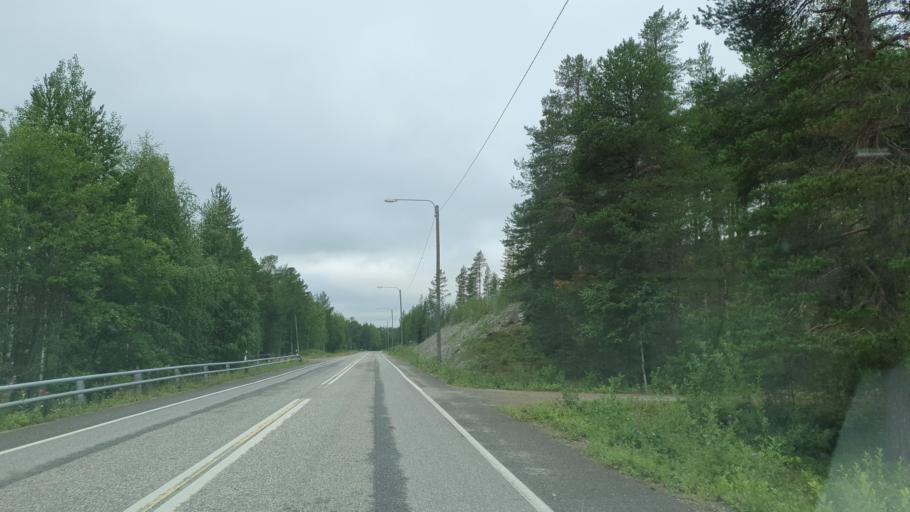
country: FI
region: Lapland
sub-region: Pohjois-Lappi
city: Sodankylae
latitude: 67.3741
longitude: 26.8754
